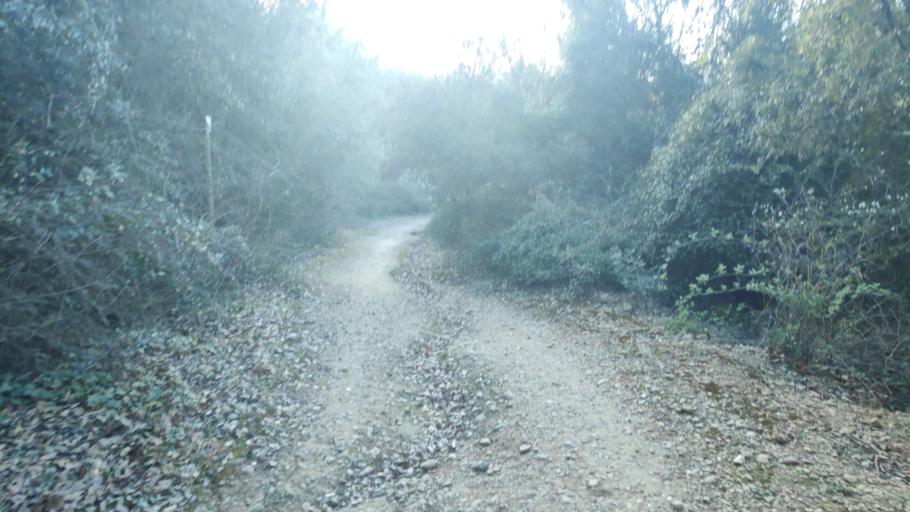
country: ES
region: Catalonia
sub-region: Provincia de Barcelona
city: Sant Quirze del Valles
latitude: 41.5323
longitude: 2.0676
